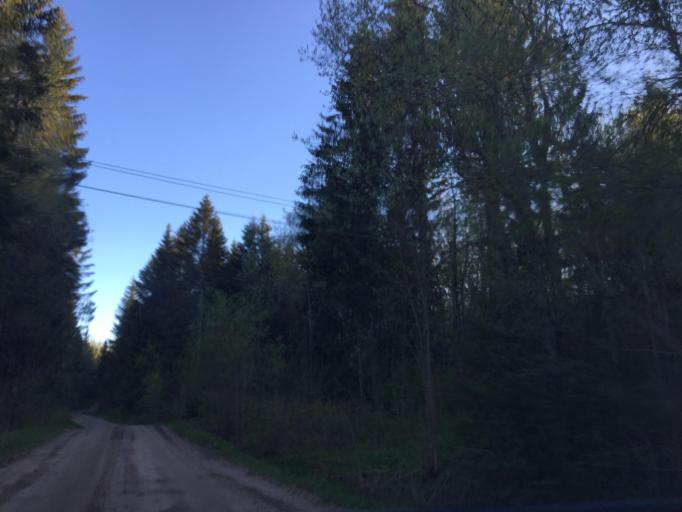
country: LV
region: Vecpiebalga
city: Vecpiebalga
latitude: 56.8543
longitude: 25.9571
